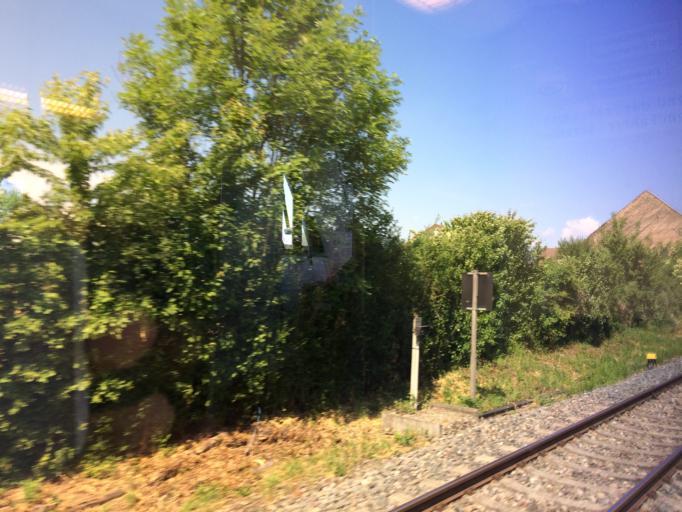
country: DE
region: Baden-Wuerttemberg
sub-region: Tuebingen Region
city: Meckenbeuren
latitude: 47.6789
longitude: 9.5384
